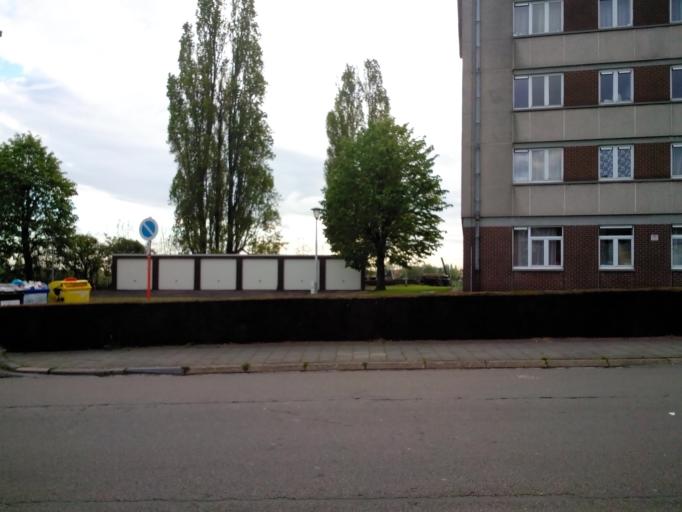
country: BE
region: Flanders
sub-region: Provincie Vlaams-Brabant
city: Diegem
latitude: 50.8640
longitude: 4.4244
